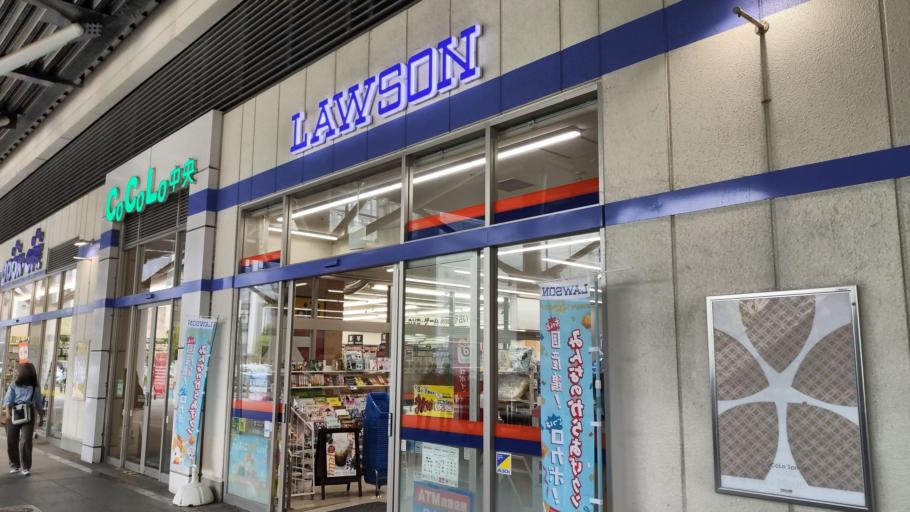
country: JP
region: Niigata
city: Niigata-shi
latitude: 37.9117
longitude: 139.0618
